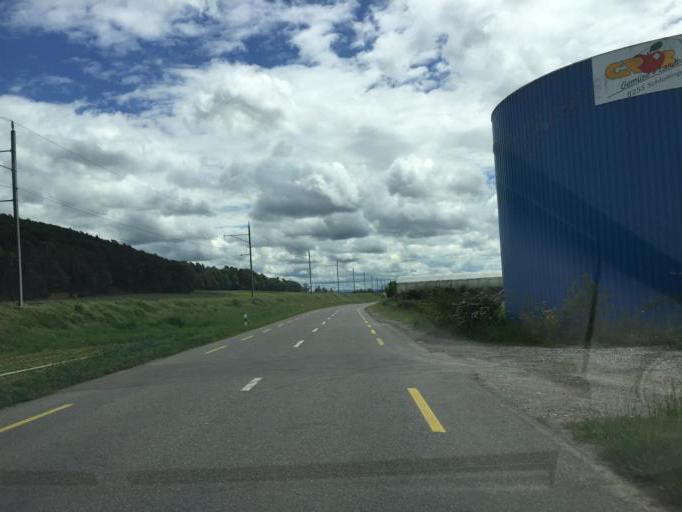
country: CH
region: Thurgau
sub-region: Frauenfeld District
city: Diessenhofen
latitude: 47.6757
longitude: 8.7630
